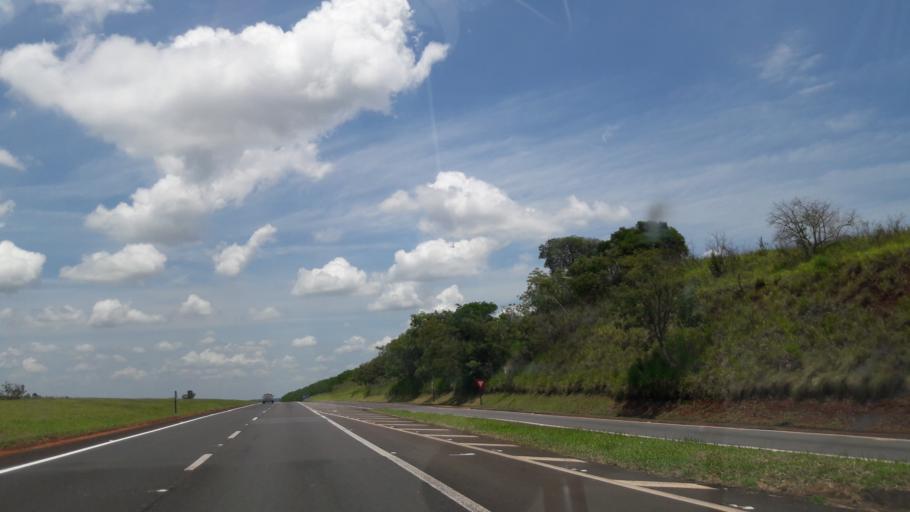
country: BR
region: Sao Paulo
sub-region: Avare
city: Avare
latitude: -22.9593
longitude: -48.8144
